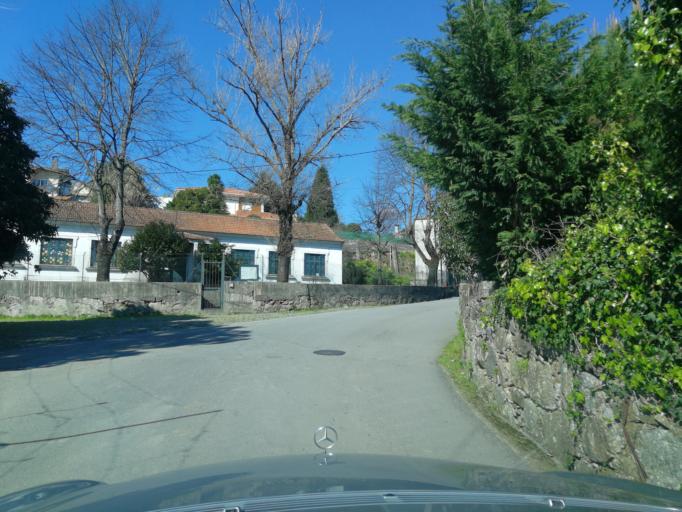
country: PT
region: Braga
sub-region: Vila Nova de Famalicao
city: Calendario
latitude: 41.3970
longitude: -8.5267
